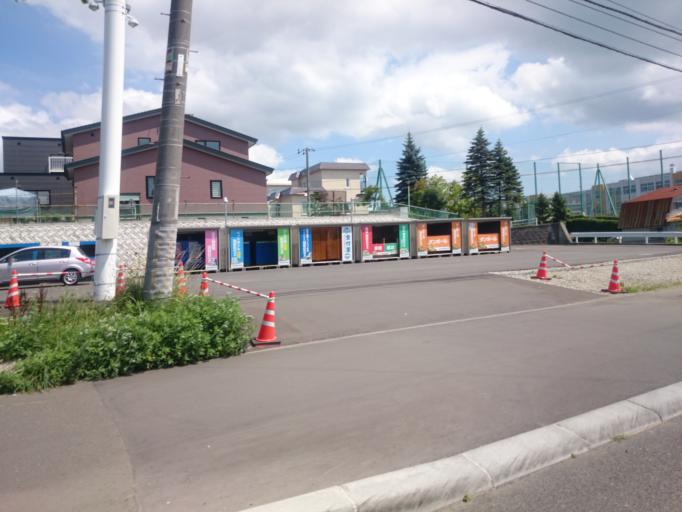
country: JP
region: Hokkaido
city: Ebetsu
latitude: 43.0563
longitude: 141.4851
